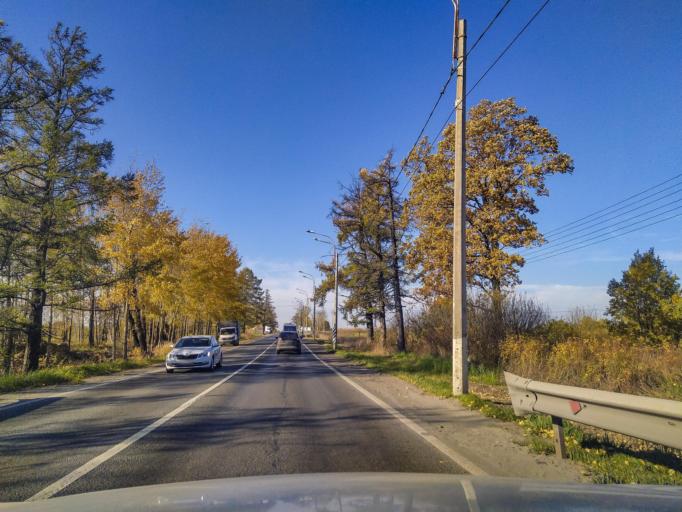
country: RU
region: St.-Petersburg
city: Aleksandrovskaya
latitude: 59.7083
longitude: 30.3284
